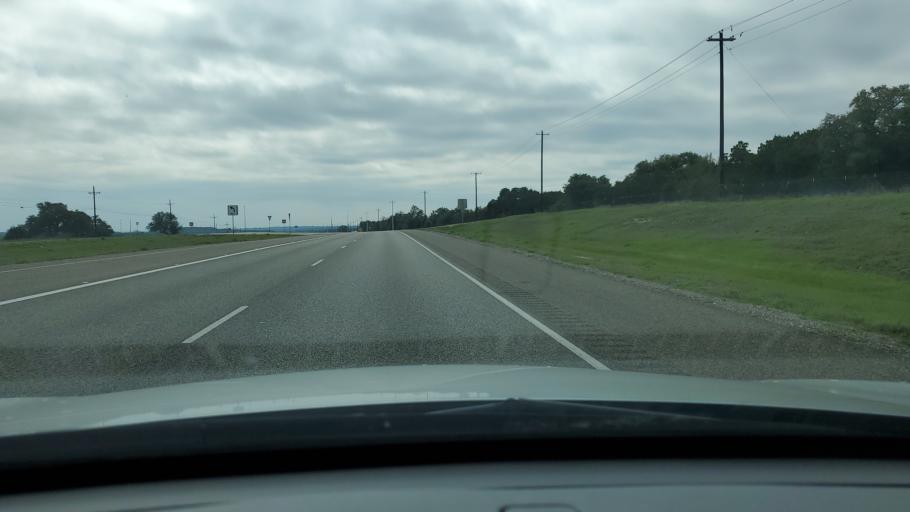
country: US
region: Texas
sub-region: Williamson County
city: Florence
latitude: 30.7949
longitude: -97.7674
